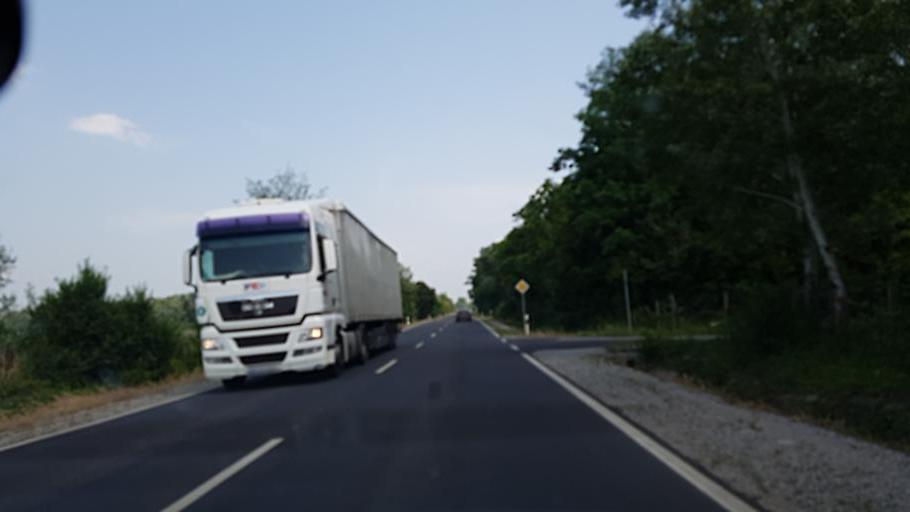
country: HU
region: Heves
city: Besenyotelek
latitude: 47.6751
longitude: 20.5302
